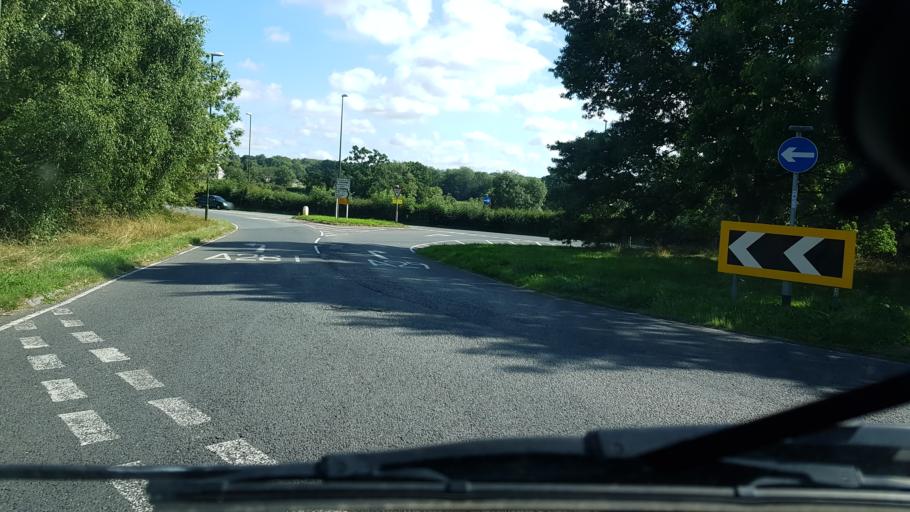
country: GB
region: England
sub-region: Surrey
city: Ockley
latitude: 51.0897
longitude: -0.3869
